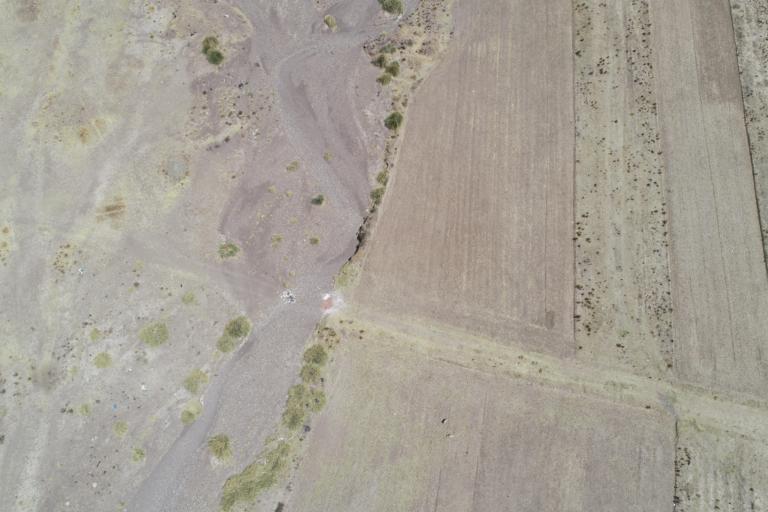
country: BO
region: La Paz
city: Achacachi
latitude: -15.9121
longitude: -68.8829
